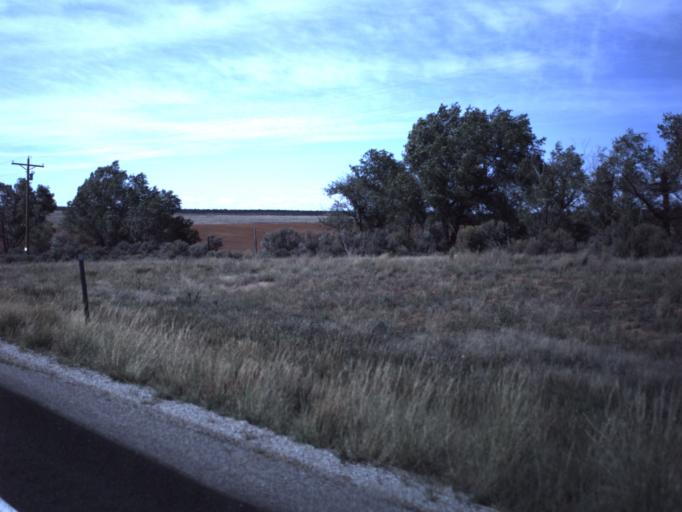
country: US
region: Utah
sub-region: San Juan County
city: Monticello
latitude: 37.8471
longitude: -109.1513
